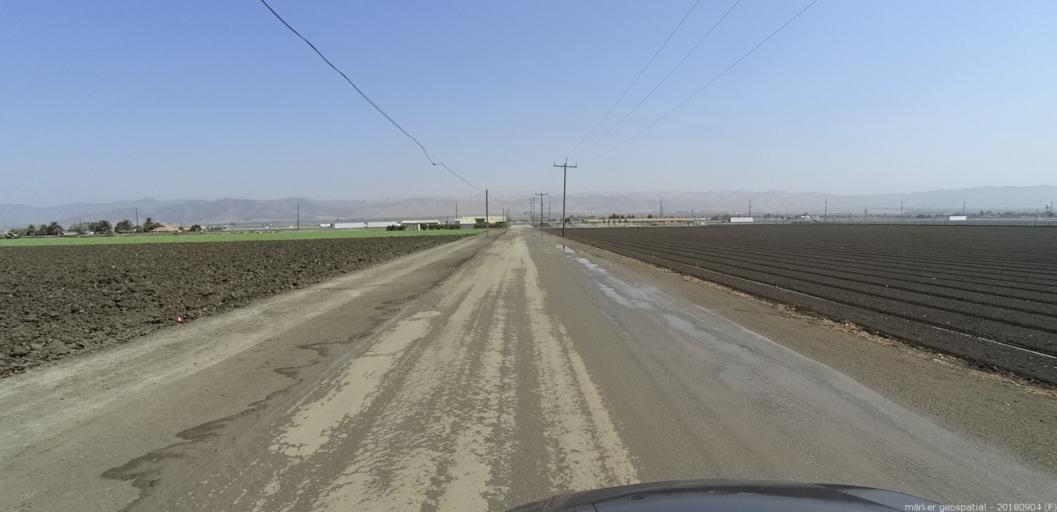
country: US
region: California
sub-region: Monterey County
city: Gonzales
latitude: 36.5166
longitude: -121.4625
